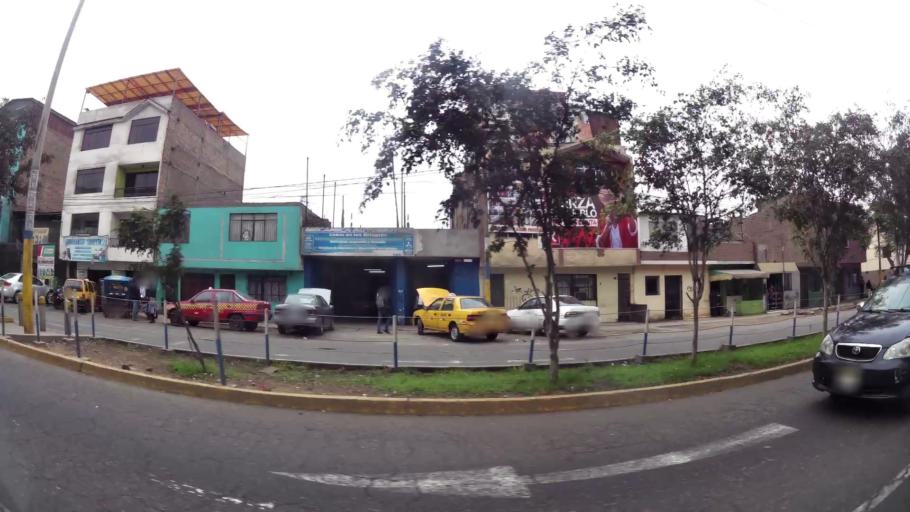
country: PE
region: Lima
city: Lima
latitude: -12.0217
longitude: -77.0061
